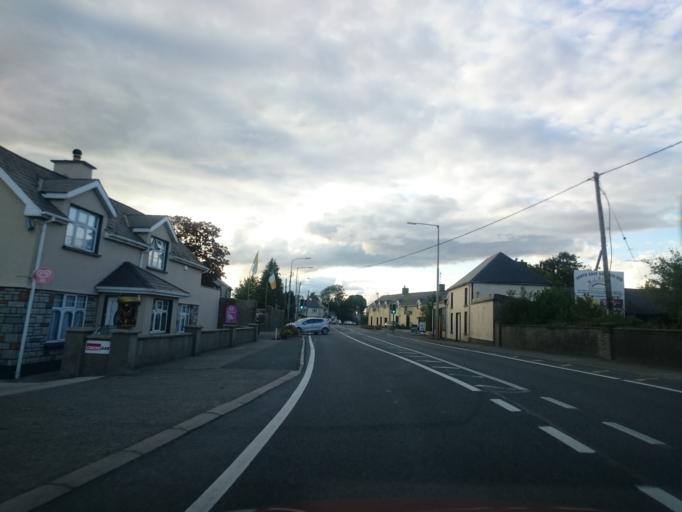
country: IE
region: Leinster
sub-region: Loch Garman
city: Enniscorthy
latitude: 52.4231
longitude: -6.5300
